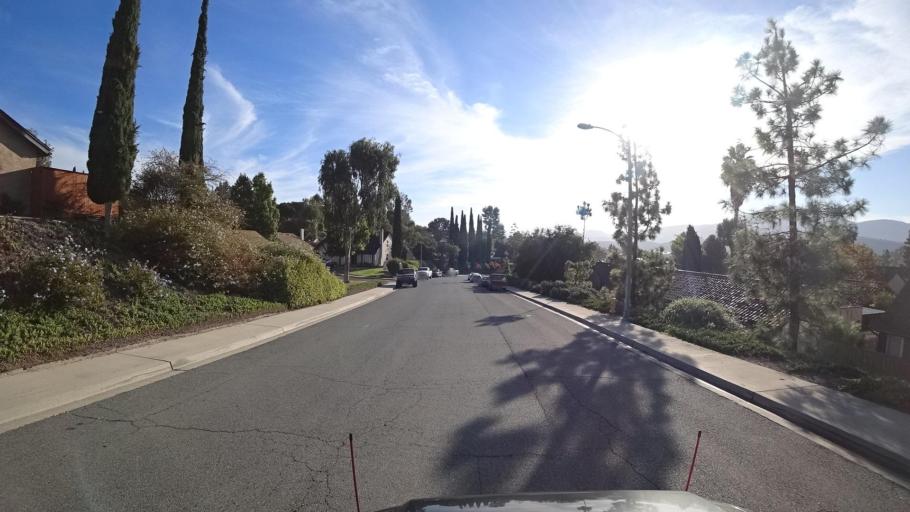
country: US
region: California
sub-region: San Diego County
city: Spring Valley
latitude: 32.7357
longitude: -116.9814
